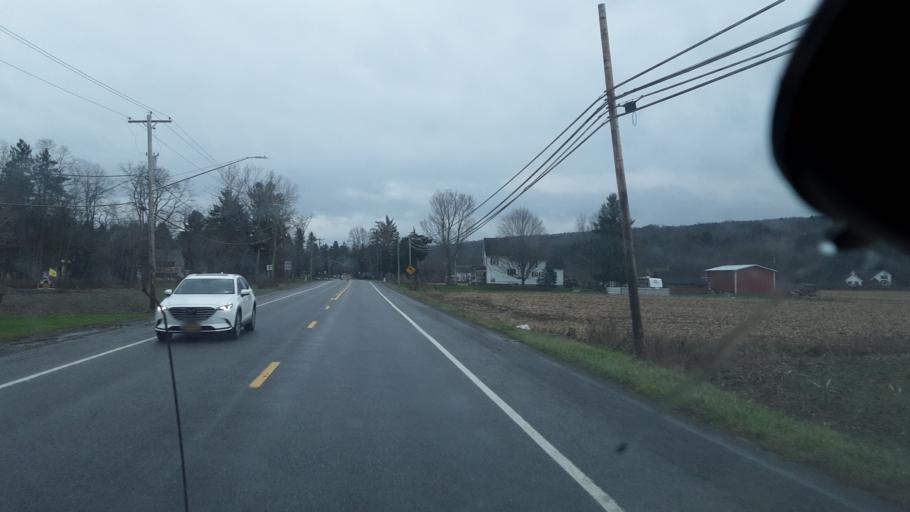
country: US
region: New York
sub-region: Erie County
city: Holland
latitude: 42.6956
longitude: -78.5719
